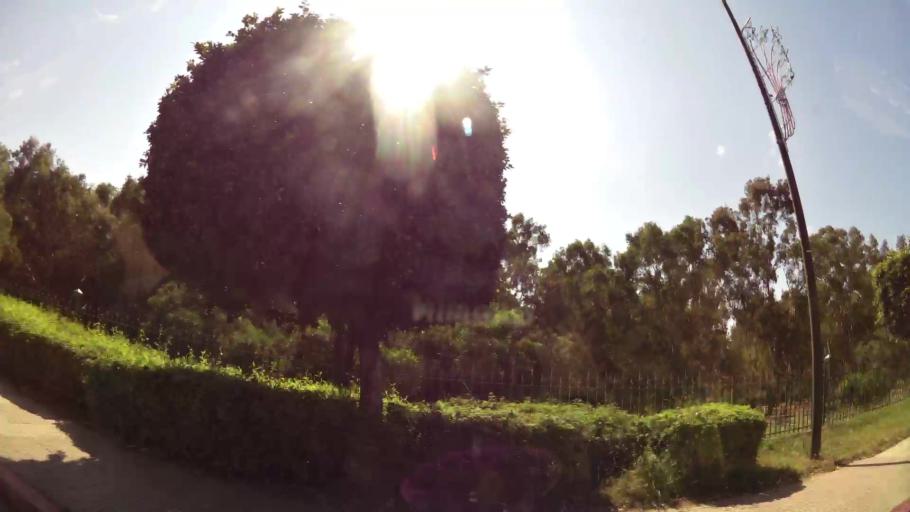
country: MA
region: Rabat-Sale-Zemmour-Zaer
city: Sale
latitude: 34.0352
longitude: -6.7757
